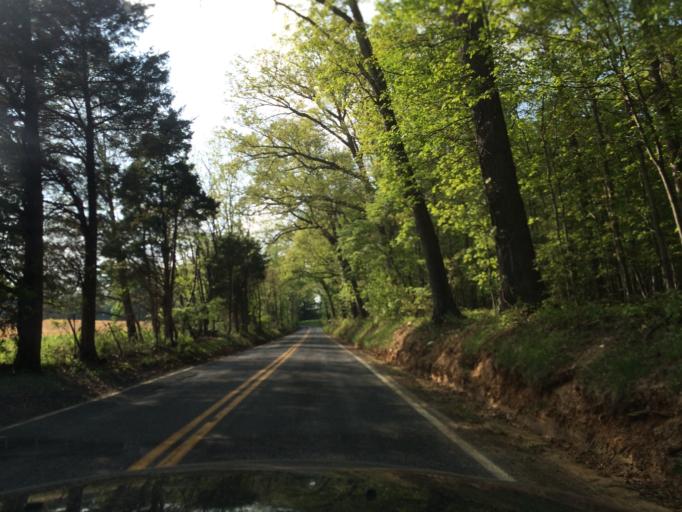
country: US
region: Maryland
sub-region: Carroll County
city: Mount Airy
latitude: 39.2994
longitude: -77.0934
